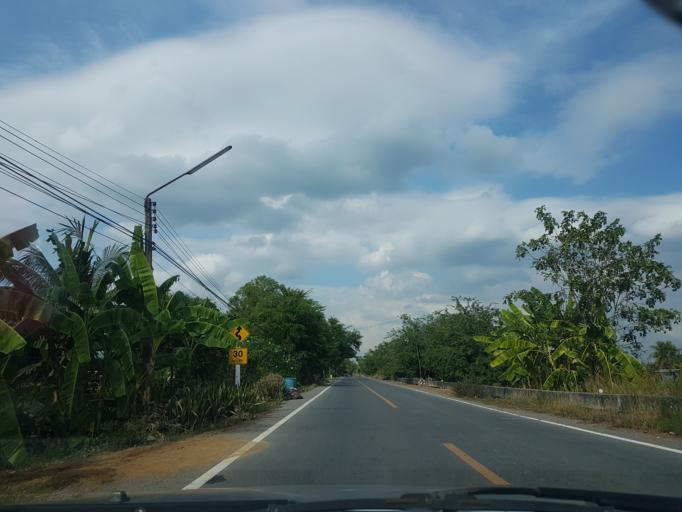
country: TH
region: Pathum Thani
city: Nong Suea
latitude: 14.1462
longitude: 100.8914
